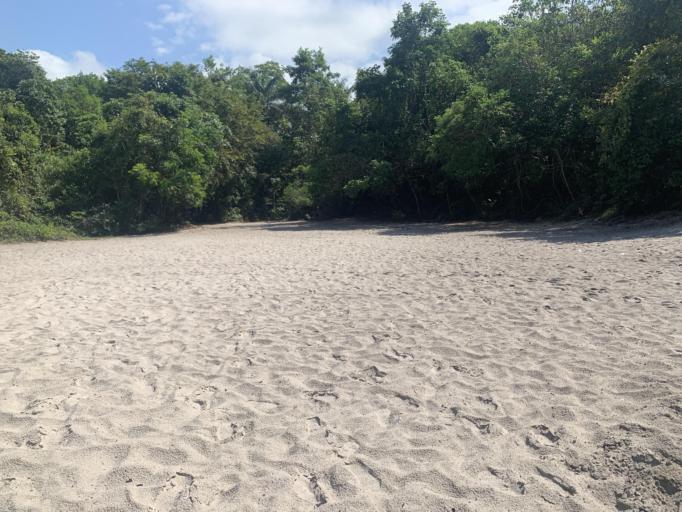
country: BR
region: Amazonas
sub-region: Manaus
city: Manaus
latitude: -3.0978
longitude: -59.9540
